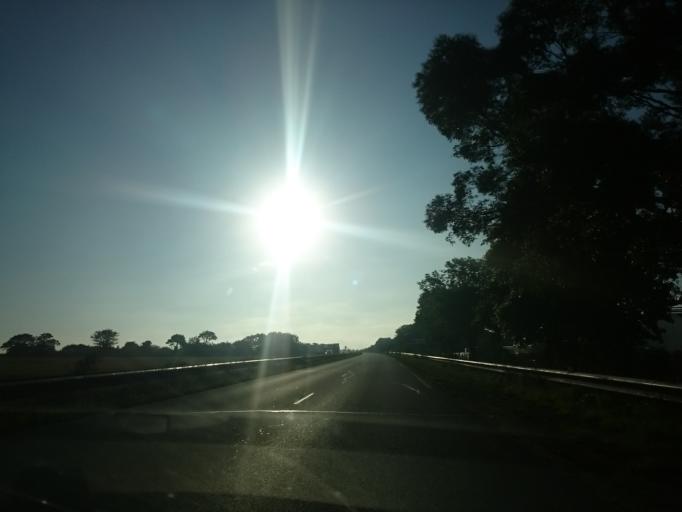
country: FR
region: Brittany
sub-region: Departement du Finistere
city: Gouesnou
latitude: 48.4331
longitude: -4.4581
